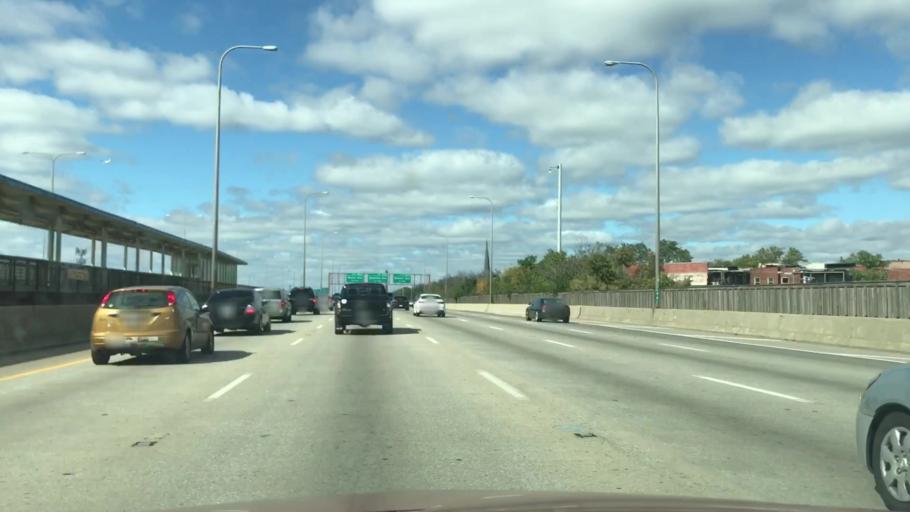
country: US
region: Illinois
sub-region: Cook County
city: Lincolnwood
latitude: 41.9545
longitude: -87.7296
